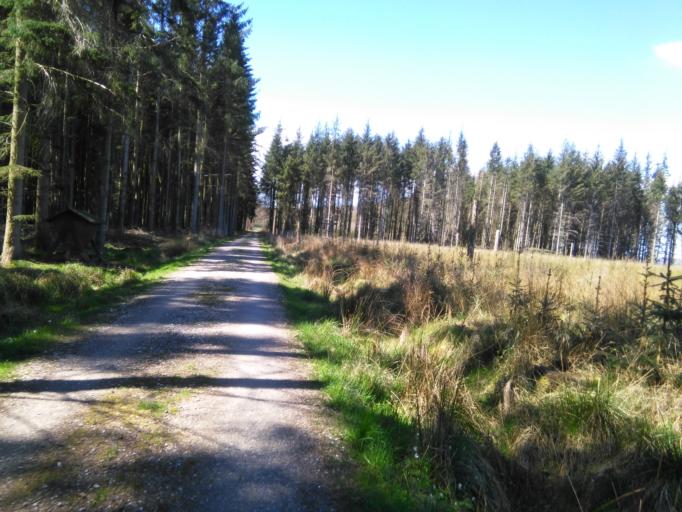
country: DK
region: Central Jutland
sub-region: Hedensted Kommune
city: Juelsminde
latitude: 55.7517
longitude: 10.0746
